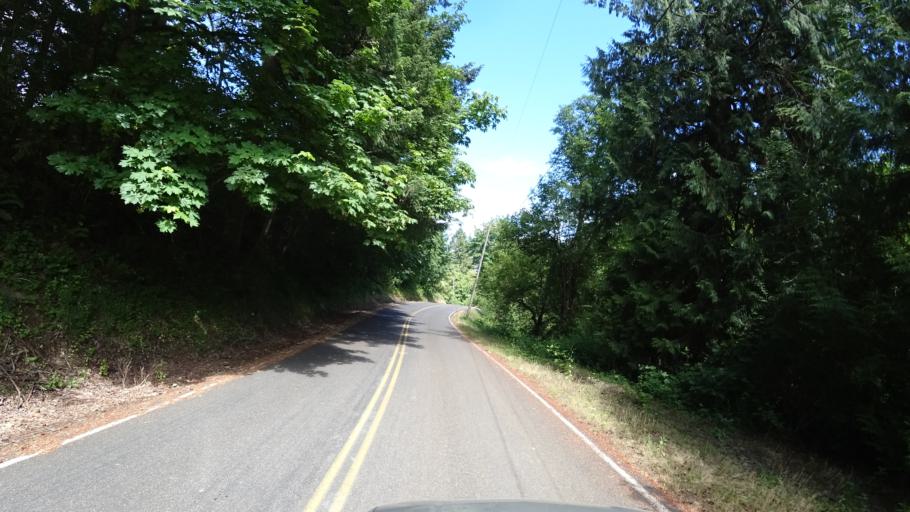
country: US
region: Oregon
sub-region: Washington County
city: Oak Hills
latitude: 45.6162
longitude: -122.8122
